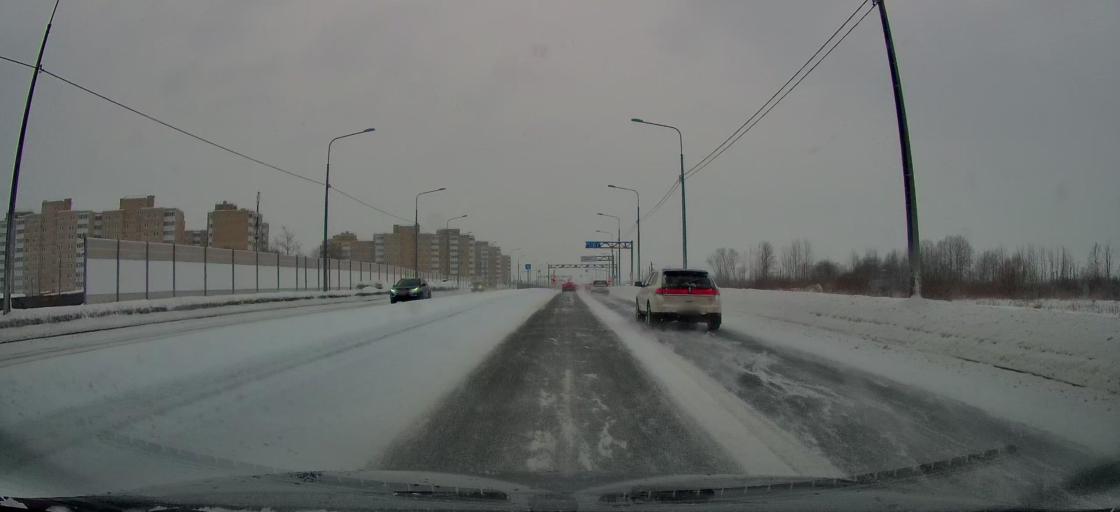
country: RU
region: St.-Petersburg
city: Krasnoye Selo
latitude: 59.7490
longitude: 30.0830
